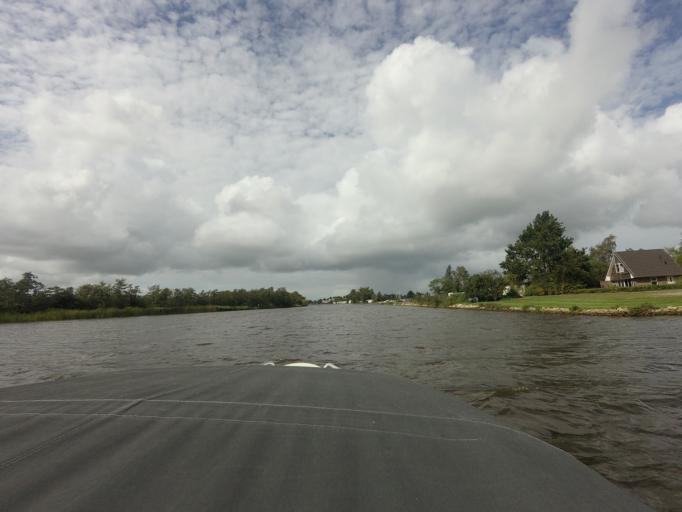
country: NL
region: Friesland
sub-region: Gemeente Boarnsterhim
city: Warten
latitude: 53.1243
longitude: 5.9404
